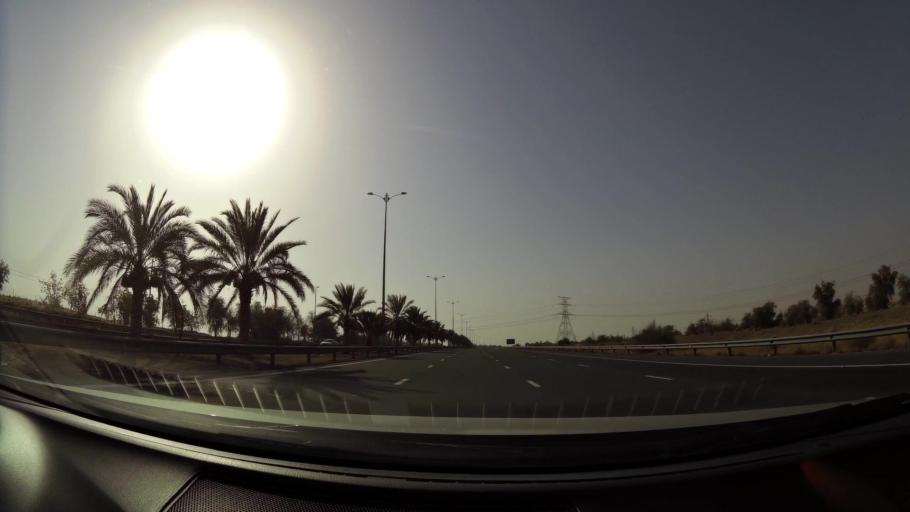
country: OM
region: Al Buraimi
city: Al Buraymi
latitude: 24.6572
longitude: 55.6922
